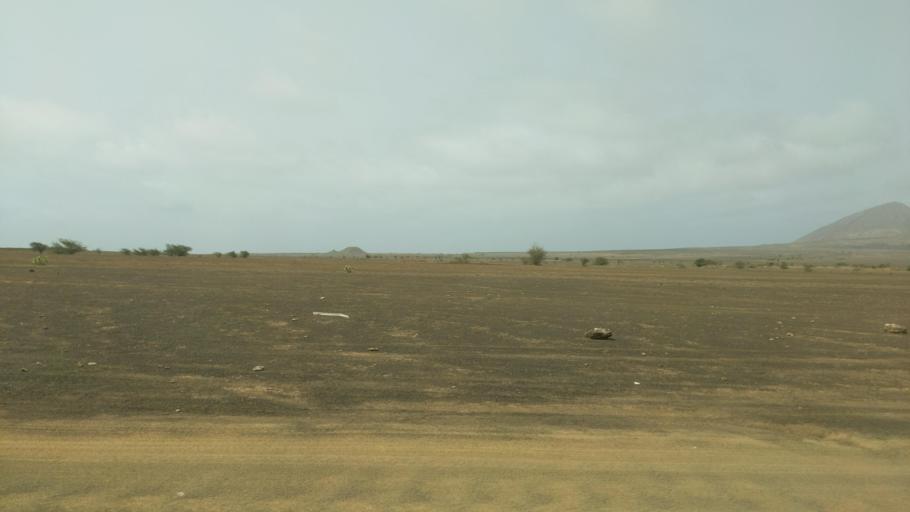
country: CV
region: Sal
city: Espargos
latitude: 16.7976
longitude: -22.9573
